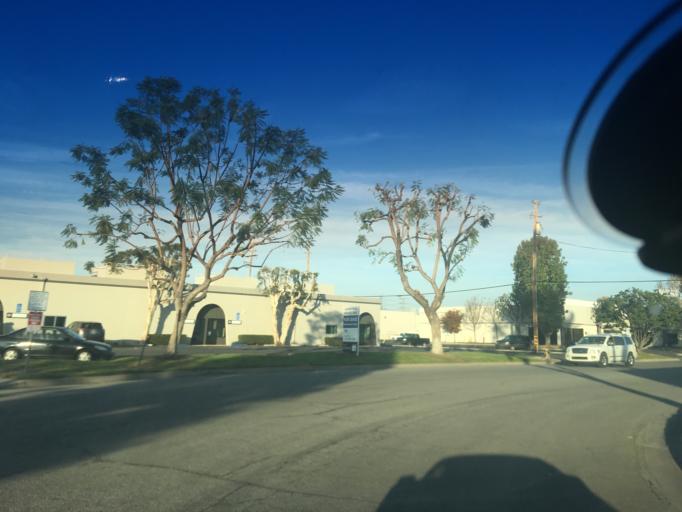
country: US
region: California
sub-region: Orange County
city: Orange
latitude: 33.8082
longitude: -117.8823
